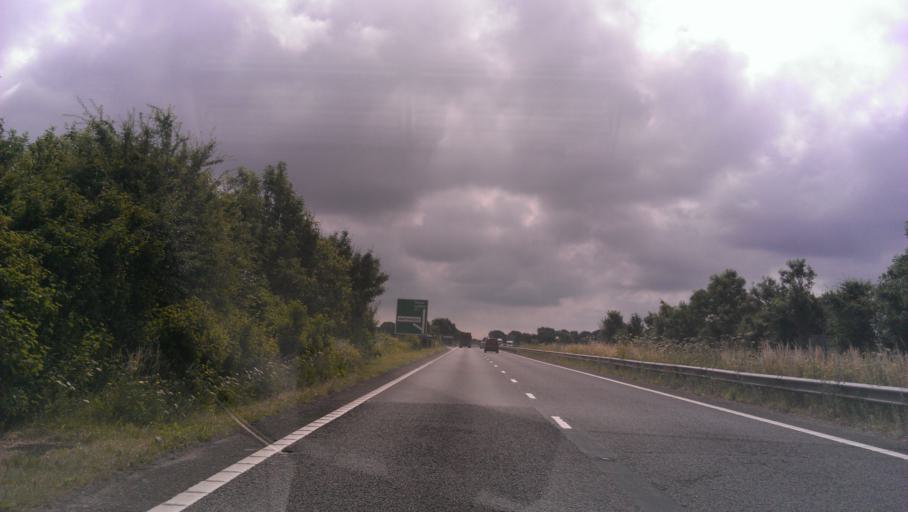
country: GB
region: England
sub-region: Kent
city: Wootton
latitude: 51.1845
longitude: 1.1957
